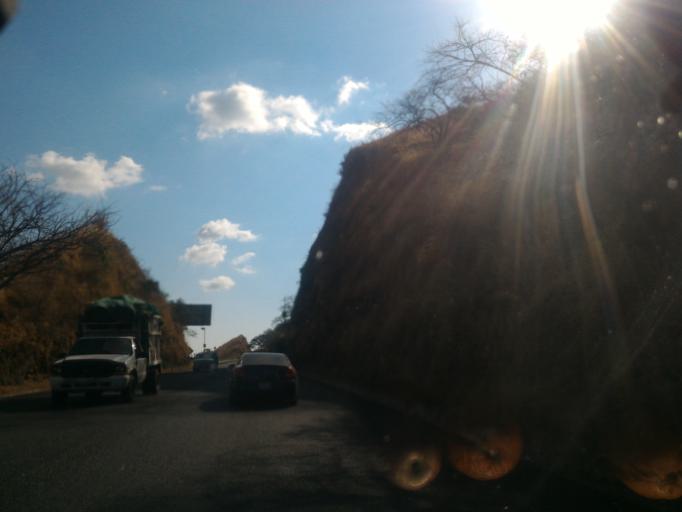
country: MX
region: Jalisco
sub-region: Tonila
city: San Marcos
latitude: 19.4586
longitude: -103.4659
